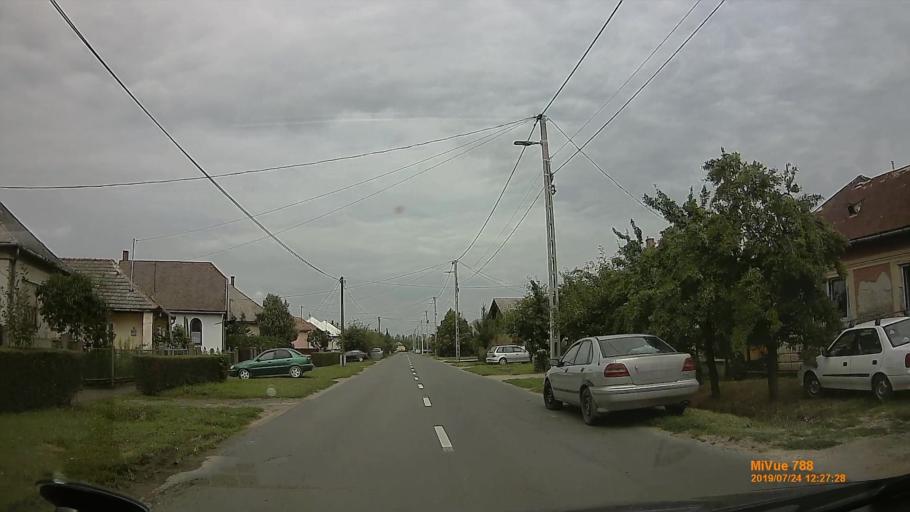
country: HU
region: Szabolcs-Szatmar-Bereg
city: Vasarosnameny
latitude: 48.1362
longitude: 22.3432
